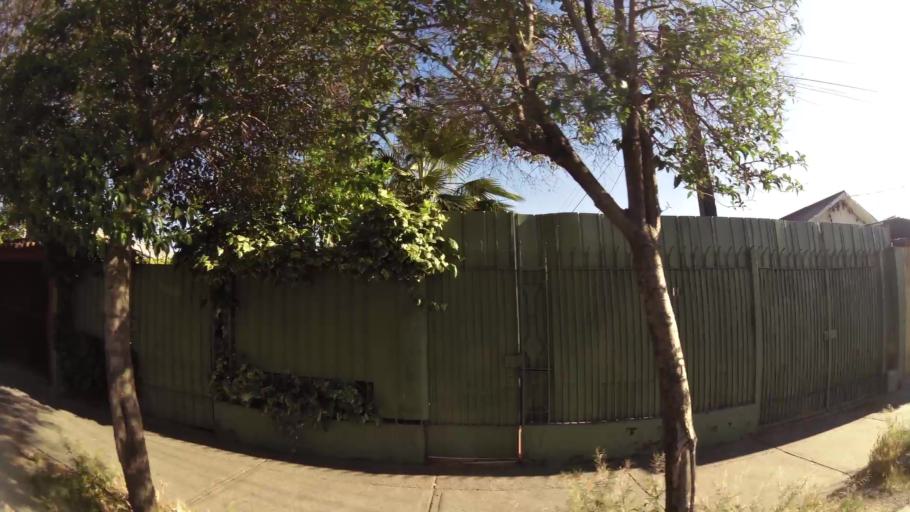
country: CL
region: Santiago Metropolitan
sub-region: Provincia de Maipo
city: San Bernardo
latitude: -33.5481
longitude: -70.6769
